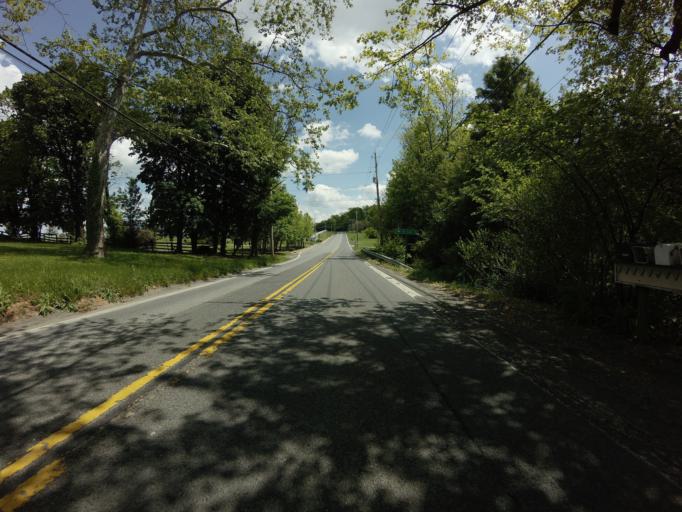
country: US
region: Maryland
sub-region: Montgomery County
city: Damascus
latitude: 39.3381
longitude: -77.2296
